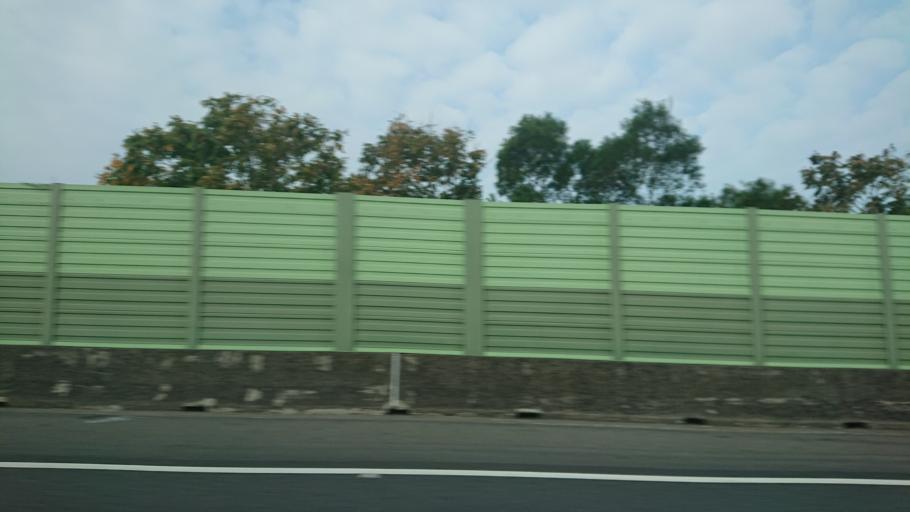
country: TW
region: Taiwan
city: Fengyuan
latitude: 24.3900
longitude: 120.6680
